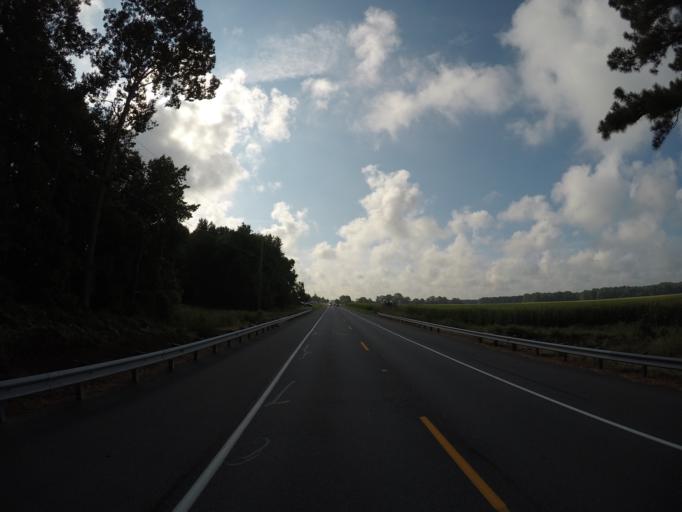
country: US
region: Delaware
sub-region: Sussex County
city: Bridgeville
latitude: 38.7767
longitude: -75.6617
